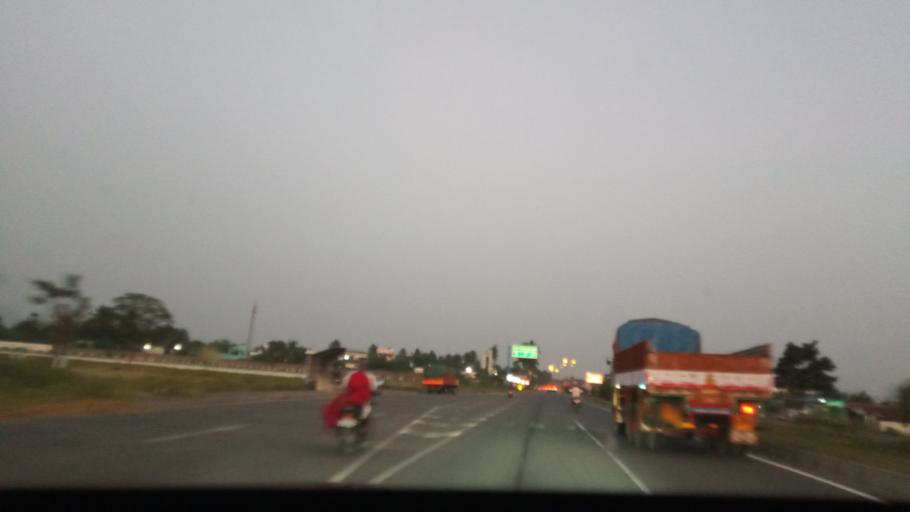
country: IN
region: Tamil Nadu
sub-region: Salem
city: Attur
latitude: 11.6173
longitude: 78.5578
